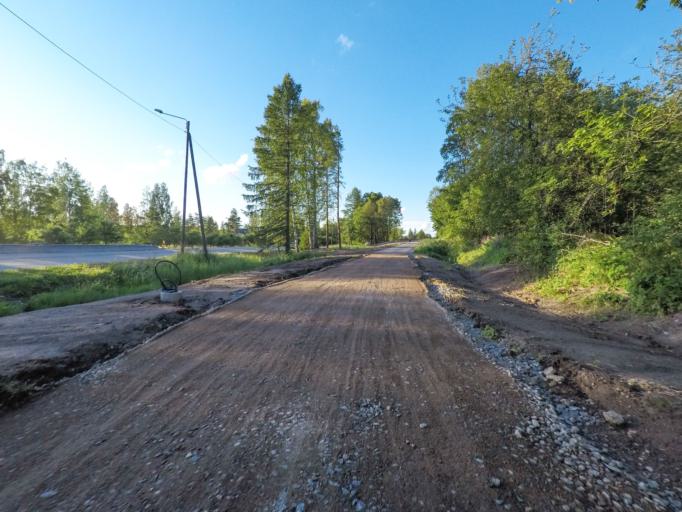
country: FI
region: South Karelia
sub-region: Imatra
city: Imatra
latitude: 61.1991
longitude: 28.7838
